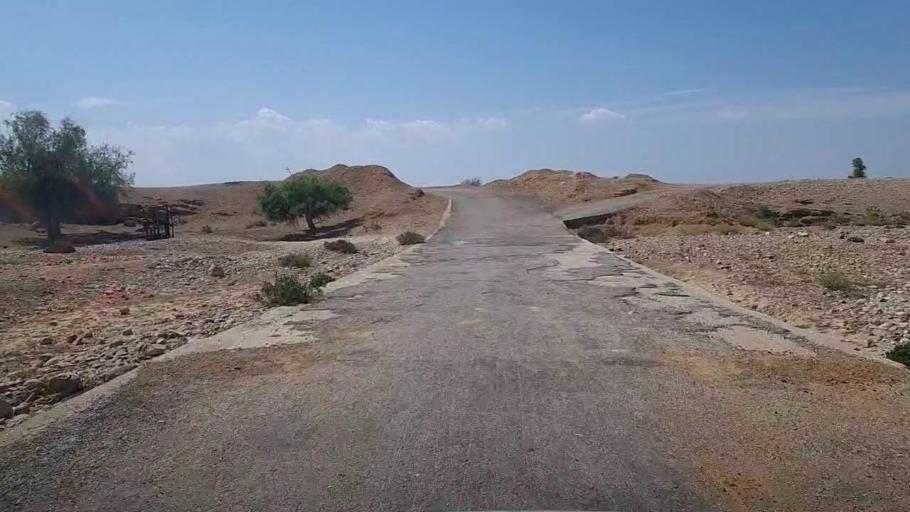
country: PK
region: Sindh
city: Bhan
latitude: 26.3794
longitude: 67.6420
